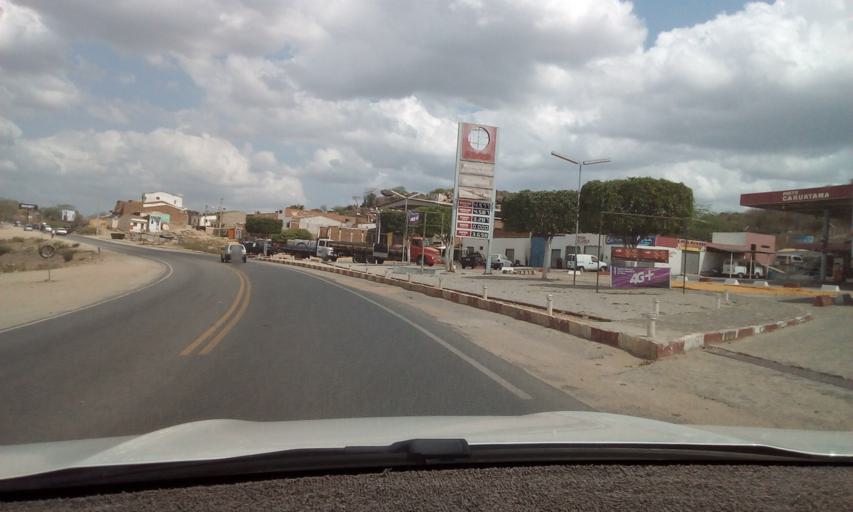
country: BR
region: Pernambuco
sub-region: Toritama
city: Toritama
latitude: -8.0139
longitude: -36.0565
